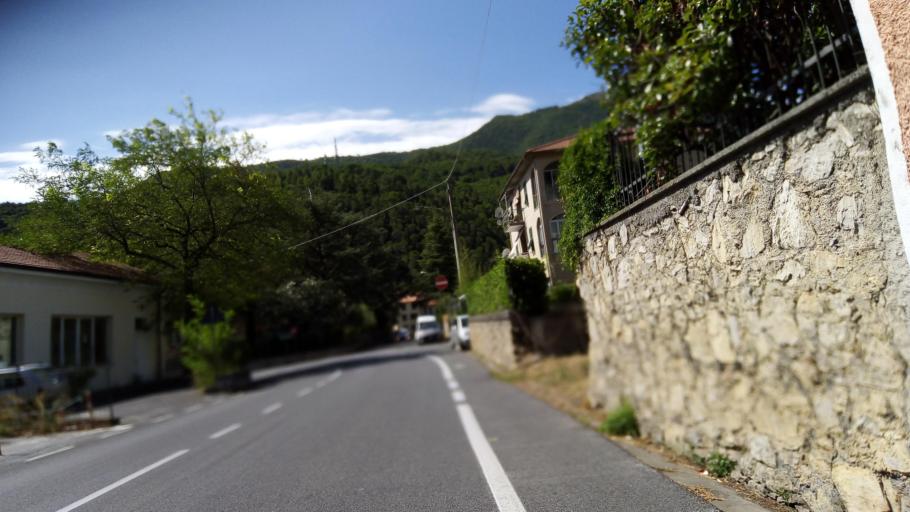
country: IT
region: Liguria
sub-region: Provincia di Savona
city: Toirano
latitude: 44.1276
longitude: 8.2048
